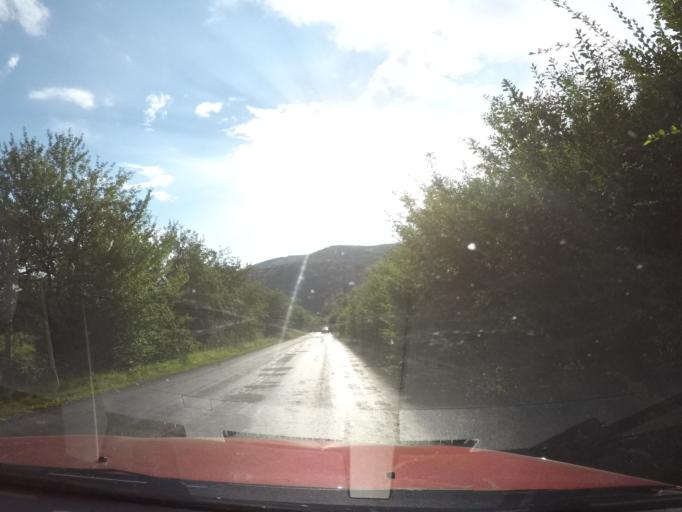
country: UA
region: Zakarpattia
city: Velykyi Bereznyi
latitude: 48.9405
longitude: 22.4758
